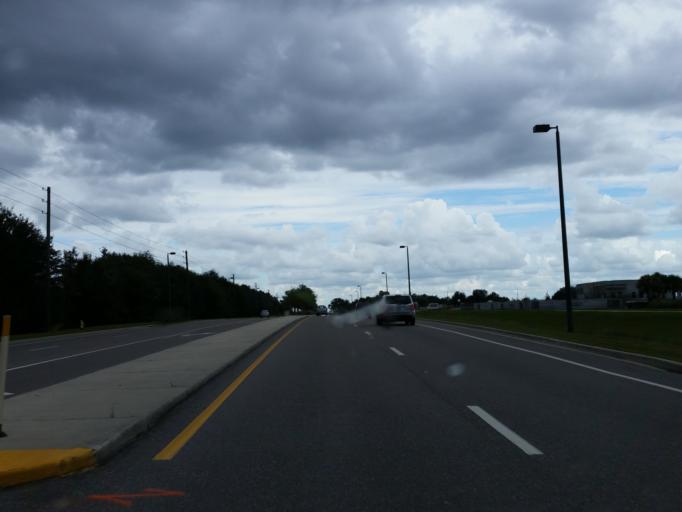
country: US
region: Florida
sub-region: Hillsborough County
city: Bloomingdale
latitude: 27.8543
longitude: -82.2598
